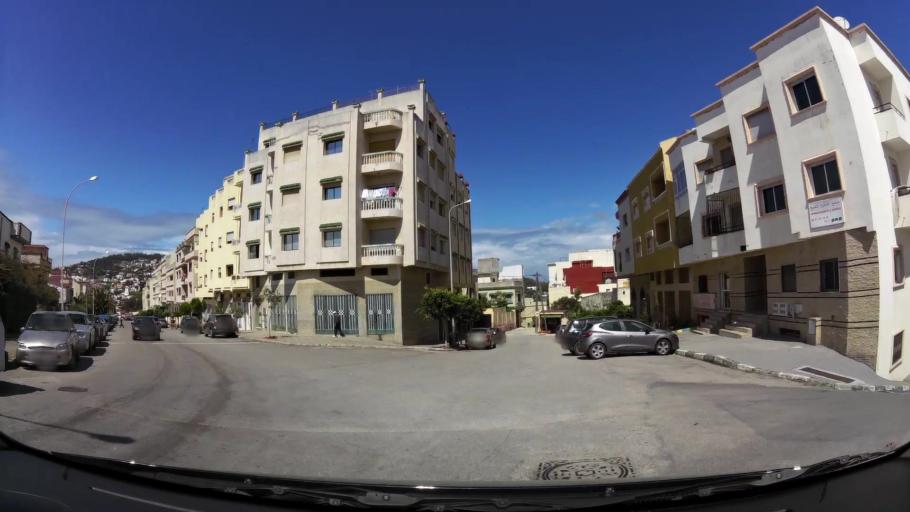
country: MA
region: Tanger-Tetouan
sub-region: Tanger-Assilah
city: Tangier
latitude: 35.7826
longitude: -5.8307
